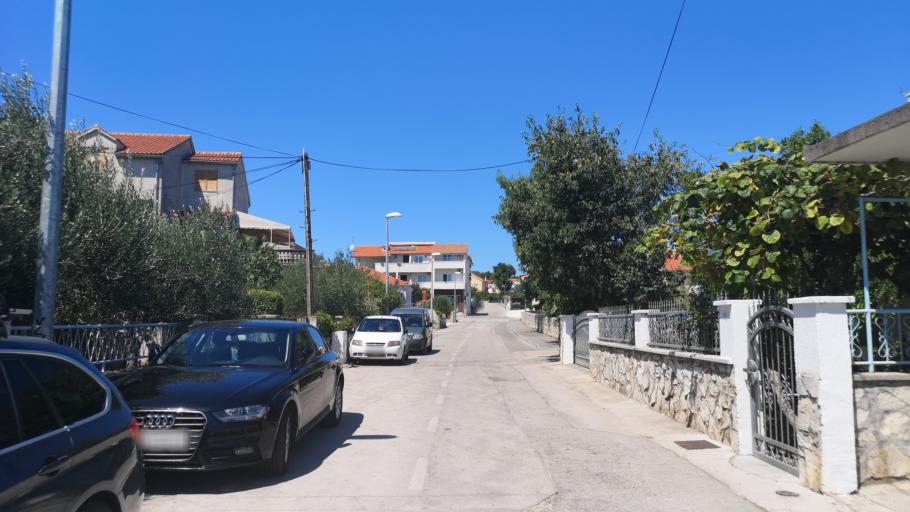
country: HR
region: Sibensko-Kniniska
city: Vodice
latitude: 43.7597
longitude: 15.7711
